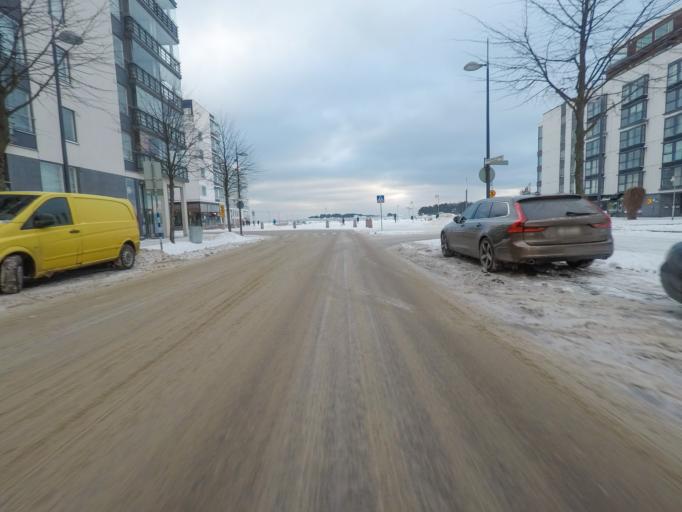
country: FI
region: Uusimaa
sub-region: Helsinki
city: Vantaa
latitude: 60.2019
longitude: 25.1493
